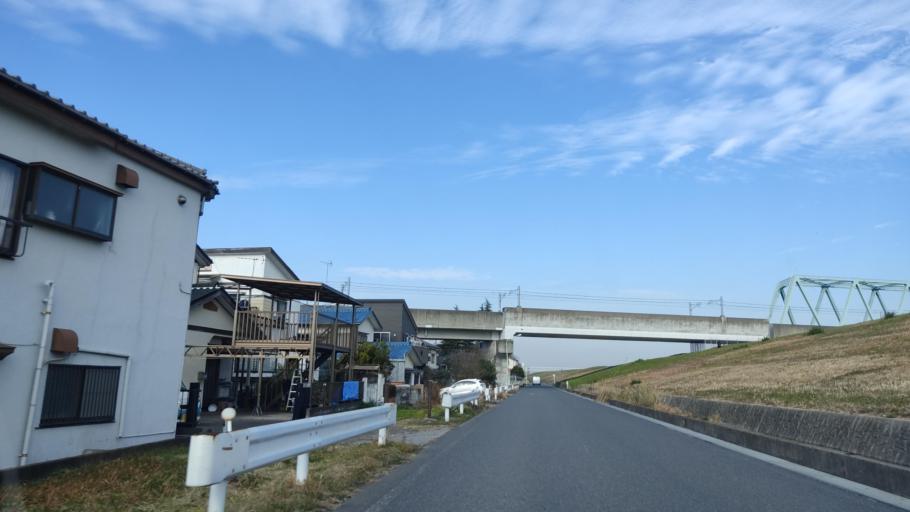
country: JP
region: Chiba
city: Nagareyama
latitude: 35.8300
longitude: 139.8858
